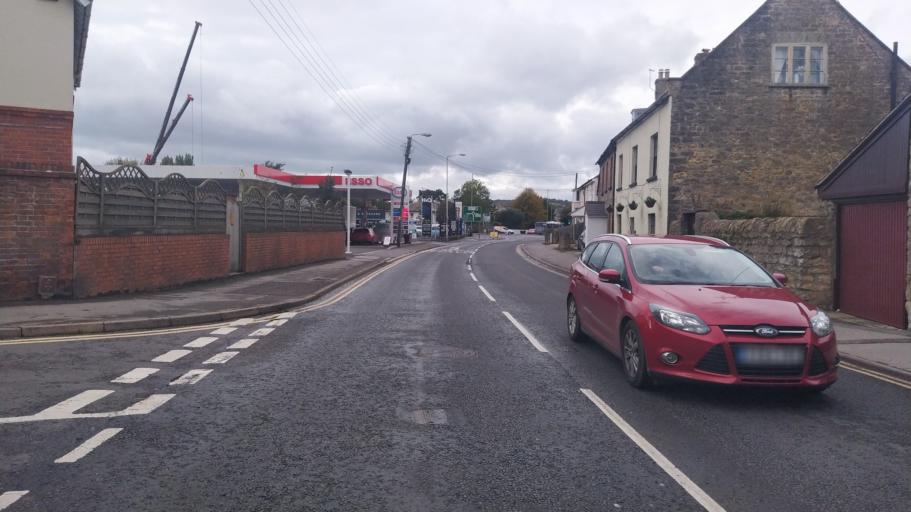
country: GB
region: England
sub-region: Dorset
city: Bridport
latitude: 50.7330
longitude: -2.7485
